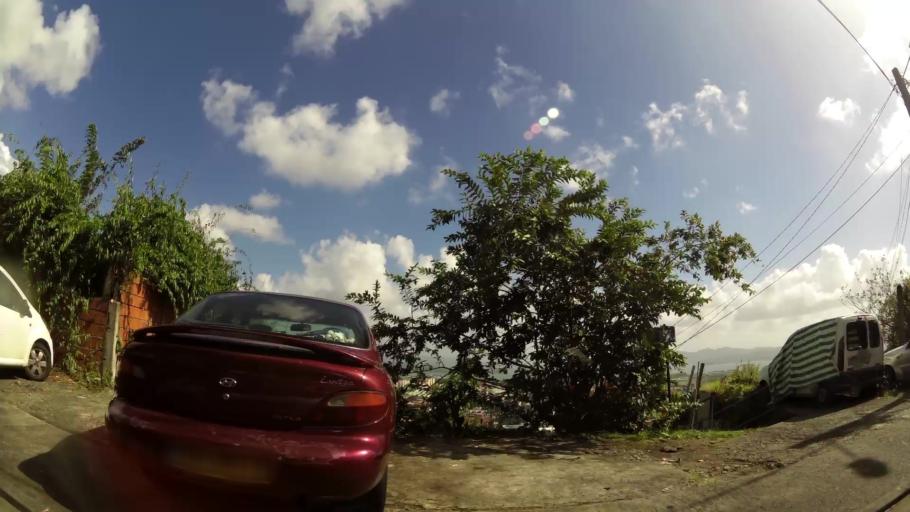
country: MQ
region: Martinique
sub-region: Martinique
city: Fort-de-France
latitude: 14.6220
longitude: -61.0544
